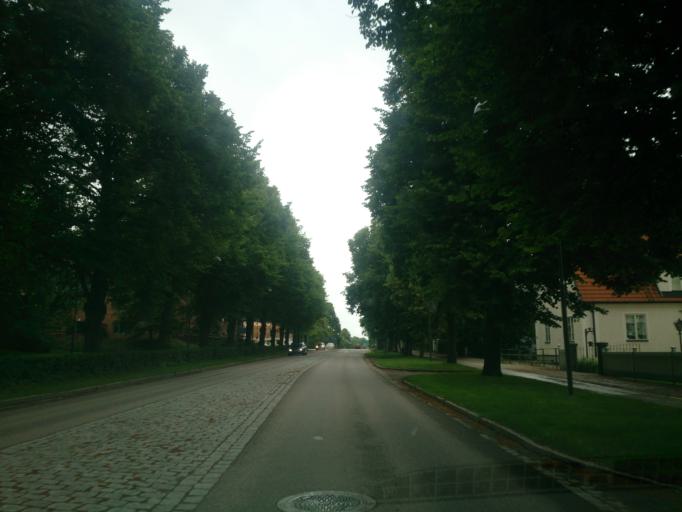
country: SE
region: OEstergoetland
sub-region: Linkopings Kommun
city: Linkoping
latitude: 58.4052
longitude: 15.6110
